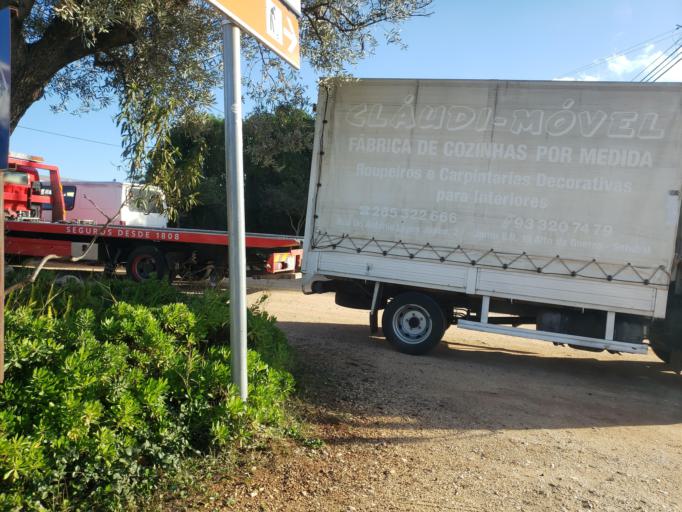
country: PT
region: Faro
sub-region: Portimao
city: Alvor
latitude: 37.1934
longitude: -8.5897
